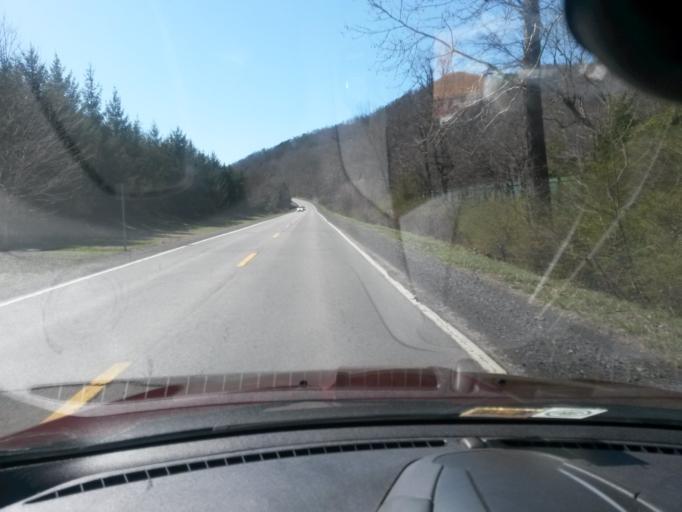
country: US
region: West Virginia
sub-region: Greenbrier County
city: White Sulphur Springs
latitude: 37.7770
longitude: -80.3386
